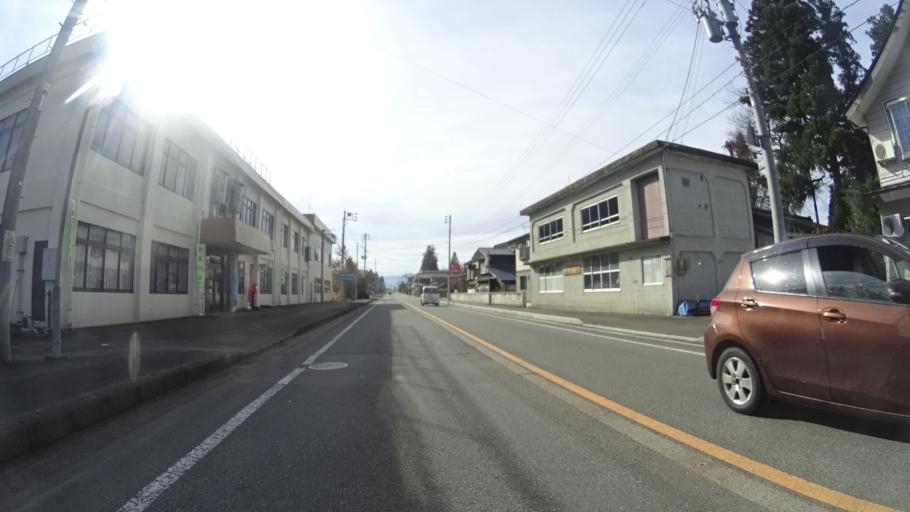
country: JP
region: Niigata
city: Muikamachi
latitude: 37.1222
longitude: 138.9268
